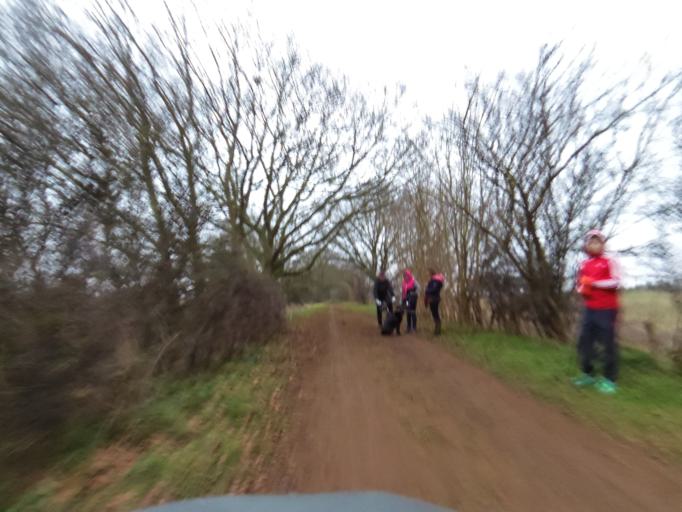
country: GB
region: England
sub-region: Norfolk
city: Horsford
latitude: 52.6992
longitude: 1.1999
